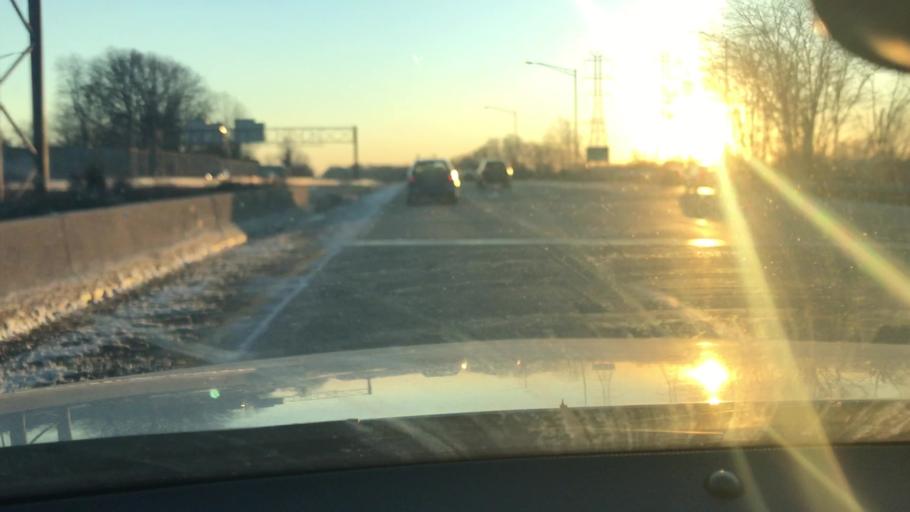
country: US
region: New Jersey
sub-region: Mercer County
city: White Horse
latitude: 40.1993
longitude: -74.7123
